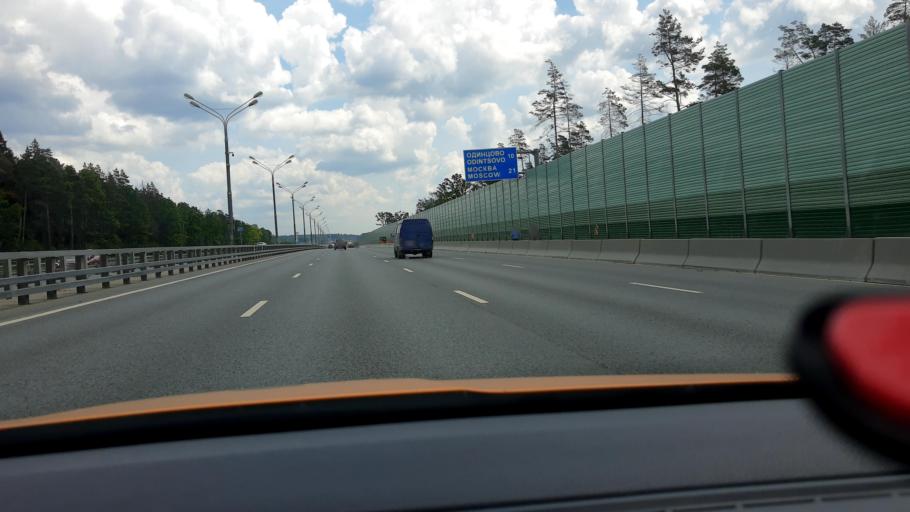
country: RU
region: Moskovskaya
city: Zhavoronki
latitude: 55.6192
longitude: 37.1132
